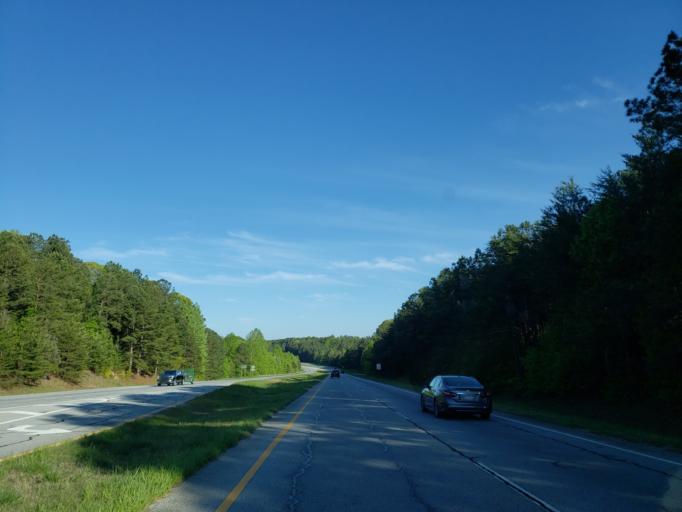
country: US
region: Georgia
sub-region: Paulding County
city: Dallas
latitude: 33.9189
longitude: -84.9289
